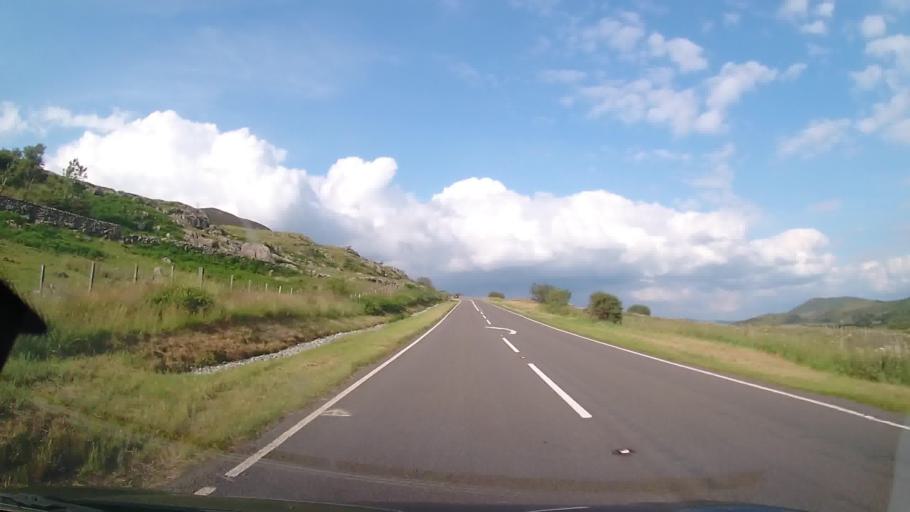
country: GB
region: Wales
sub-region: Conwy
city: Betws-y-Coed
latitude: 52.9405
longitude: -3.7588
